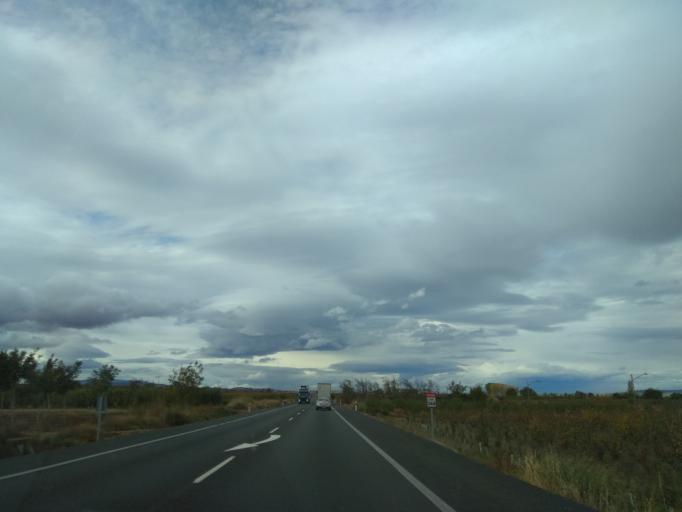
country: ES
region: La Rioja
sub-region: Provincia de La Rioja
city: Rincon de Soto
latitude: 42.2157
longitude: -1.8185
